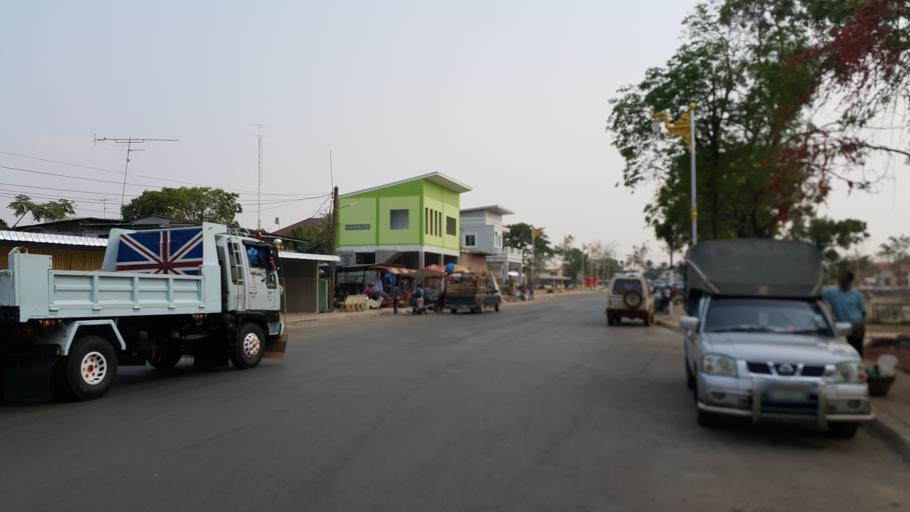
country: TH
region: Nakhon Phanom
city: That Phanom
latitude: 16.9443
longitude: 104.7272
